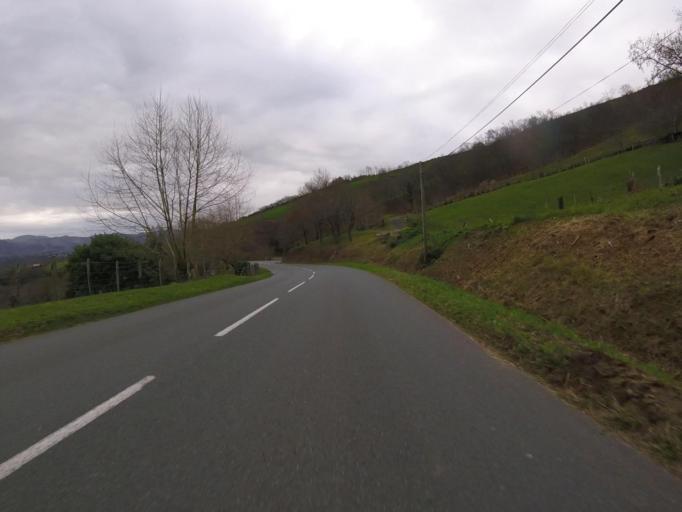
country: FR
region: Aquitaine
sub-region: Departement des Pyrenees-Atlantiques
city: Sare
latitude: 43.3184
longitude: -1.5977
